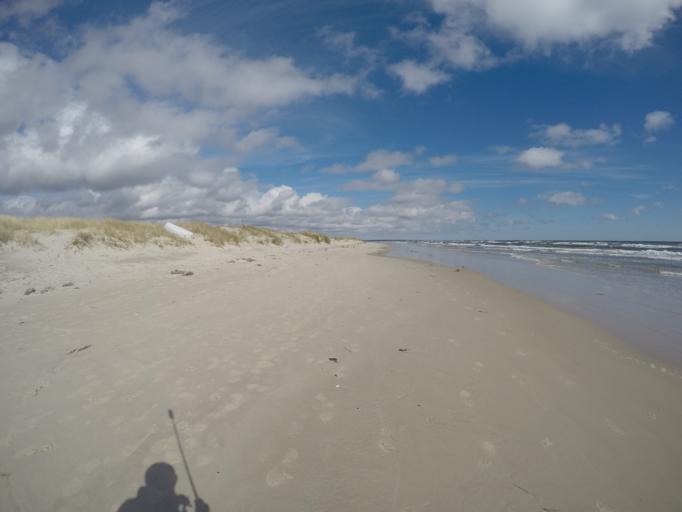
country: SE
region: Skane
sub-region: Simrishamns Kommun
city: Simrishamn
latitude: 55.3971
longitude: 14.2124
